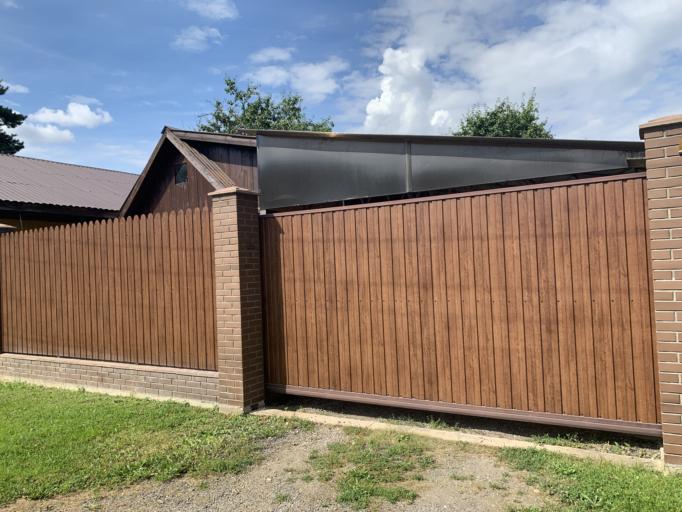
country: RU
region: Moskovskaya
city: Mamontovka
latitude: 55.9855
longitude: 37.8071
